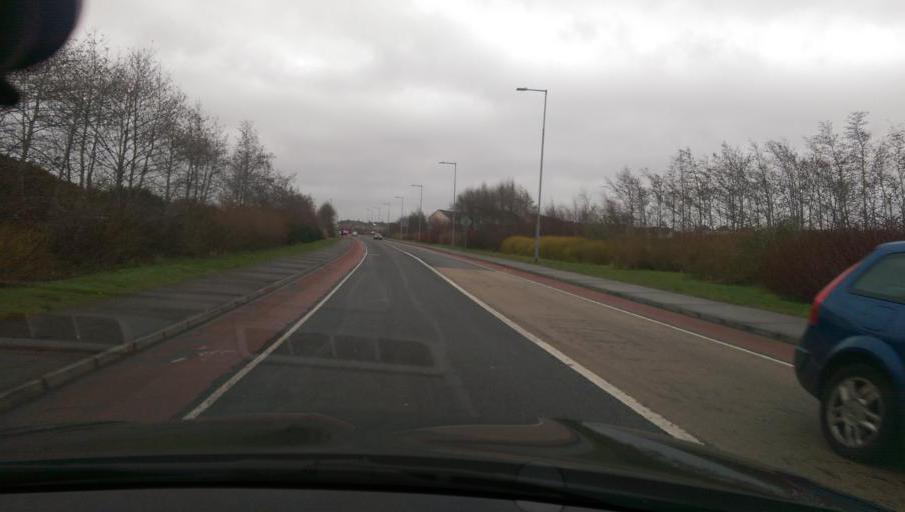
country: IE
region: Connaught
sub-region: County Galway
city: Gaillimh
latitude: 53.2700
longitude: -9.1007
